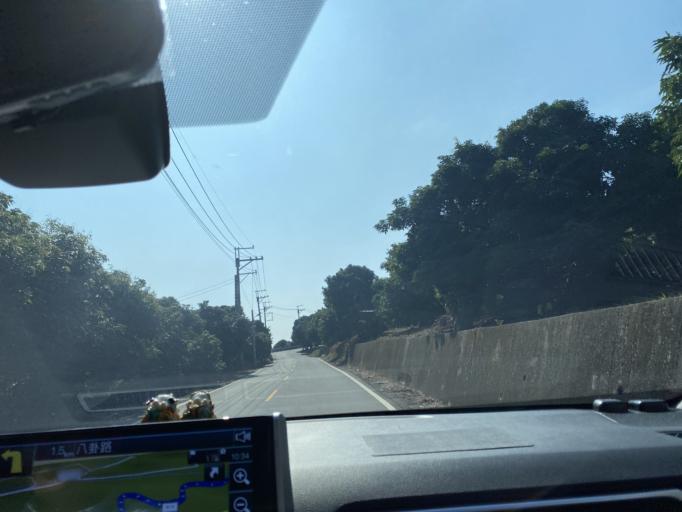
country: TW
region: Taiwan
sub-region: Nantou
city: Nantou
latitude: 23.9399
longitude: 120.6495
